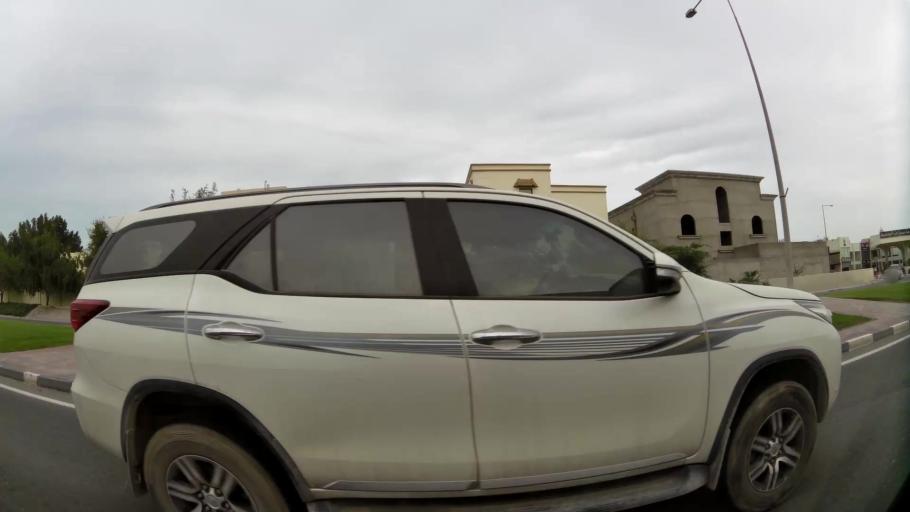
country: QA
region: Baladiyat ad Dawhah
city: Doha
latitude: 25.3375
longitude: 51.5058
